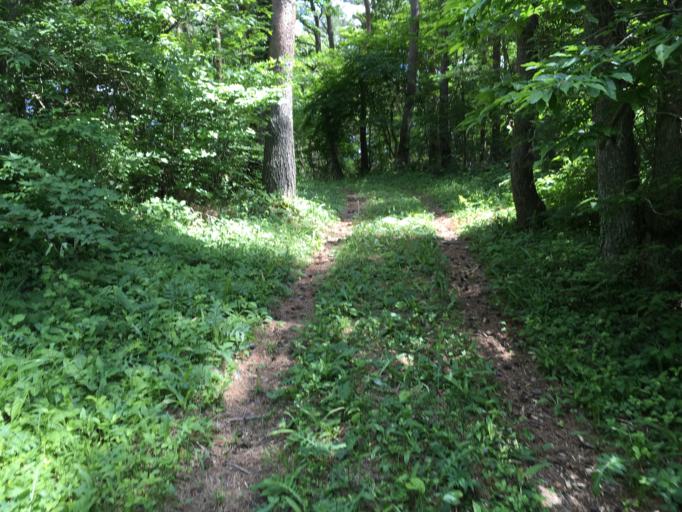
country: JP
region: Miyagi
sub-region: Oshika Gun
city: Onagawa Cho
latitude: 38.6894
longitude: 141.3558
